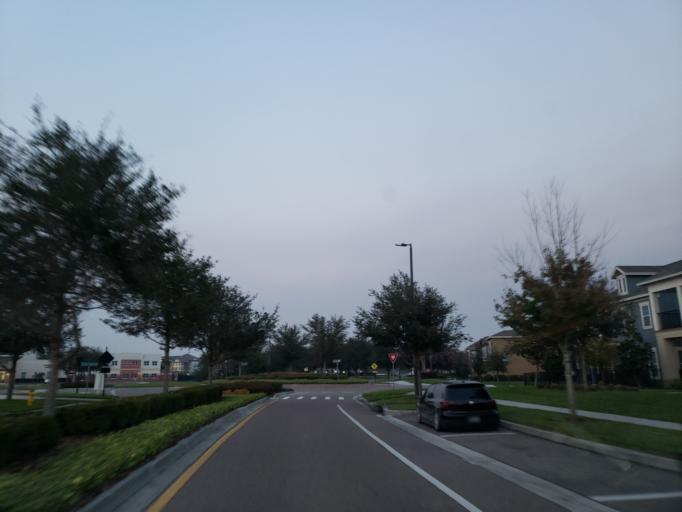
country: US
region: Florida
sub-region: Hillsborough County
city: Boyette
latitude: 27.8470
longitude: -82.2561
